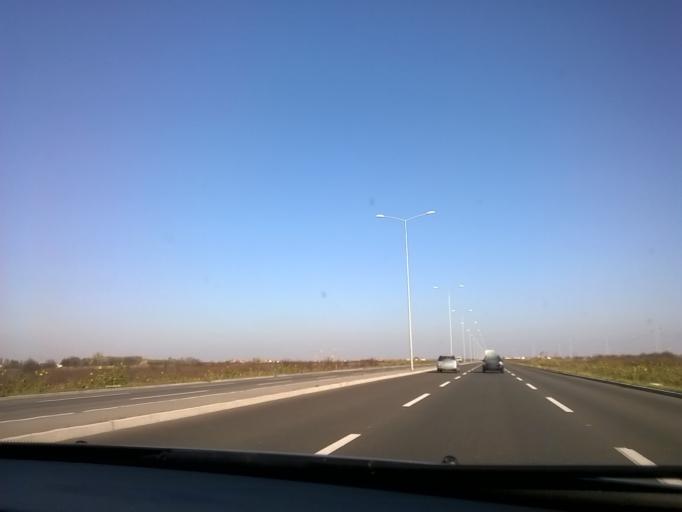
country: RS
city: Ovca
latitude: 44.8686
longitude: 20.5157
